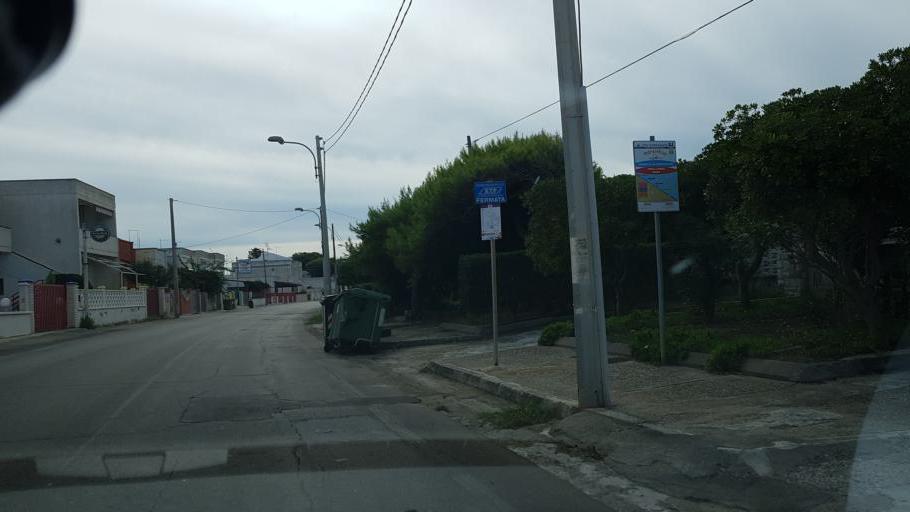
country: IT
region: Apulia
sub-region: Provincia di Lecce
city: Borgagne
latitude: 40.2928
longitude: 18.4217
